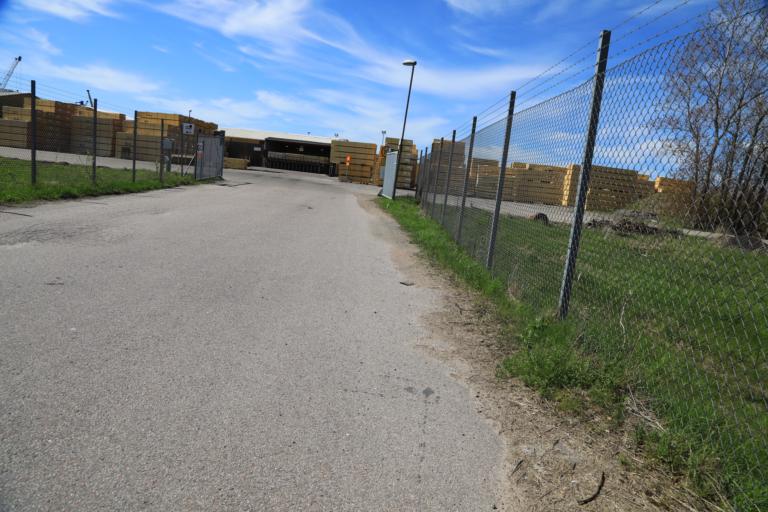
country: SE
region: Halland
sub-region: Varbergs Kommun
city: Varberg
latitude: 57.1195
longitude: 12.2488
